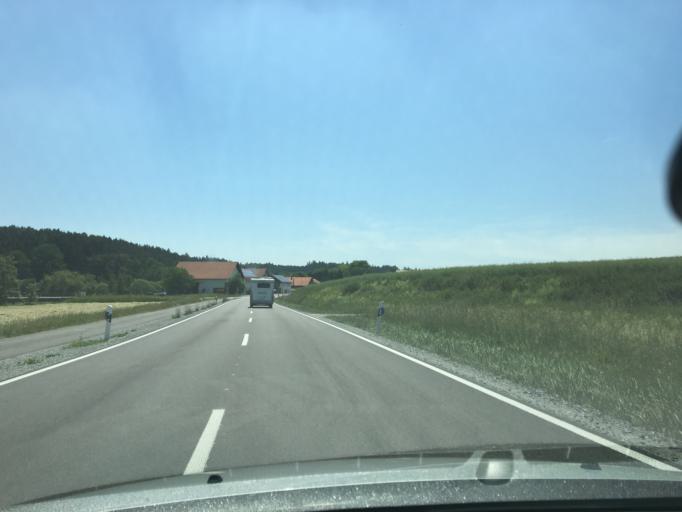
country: DE
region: Bavaria
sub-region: Upper Bavaria
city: Rohrbach
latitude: 48.3042
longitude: 12.5621
